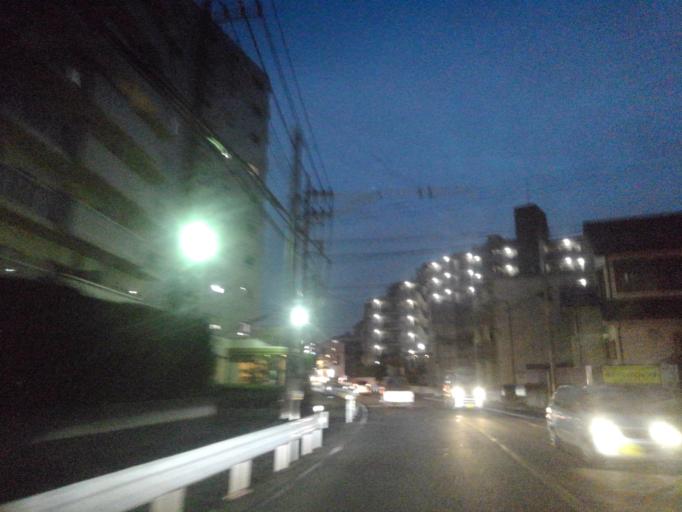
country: JP
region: Saitama
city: Tokorozawa
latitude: 35.8089
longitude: 139.4510
